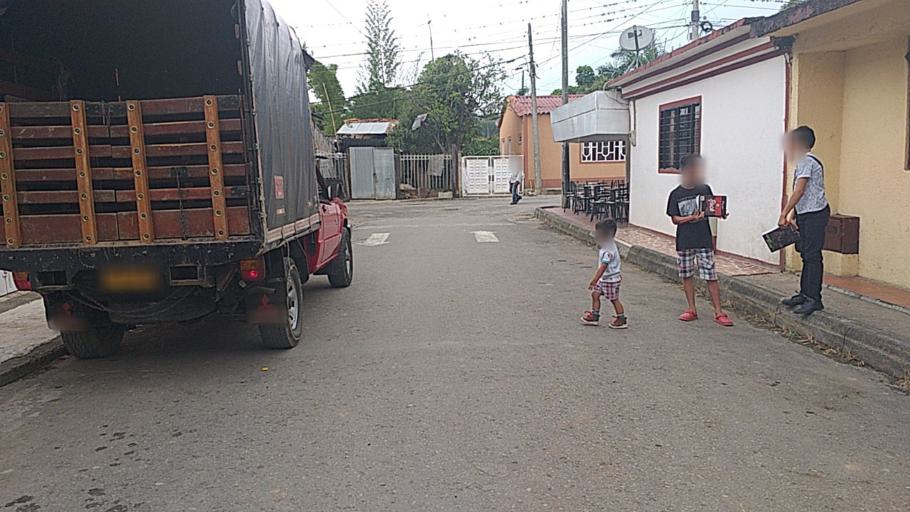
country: CO
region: Boyaca
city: Santana
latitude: 6.0584
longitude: -73.4819
